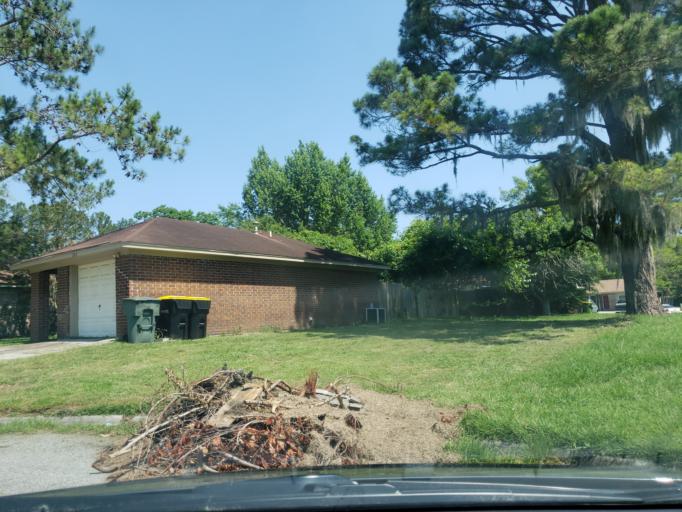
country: US
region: Georgia
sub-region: Chatham County
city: Montgomery
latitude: 31.9955
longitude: -81.1325
